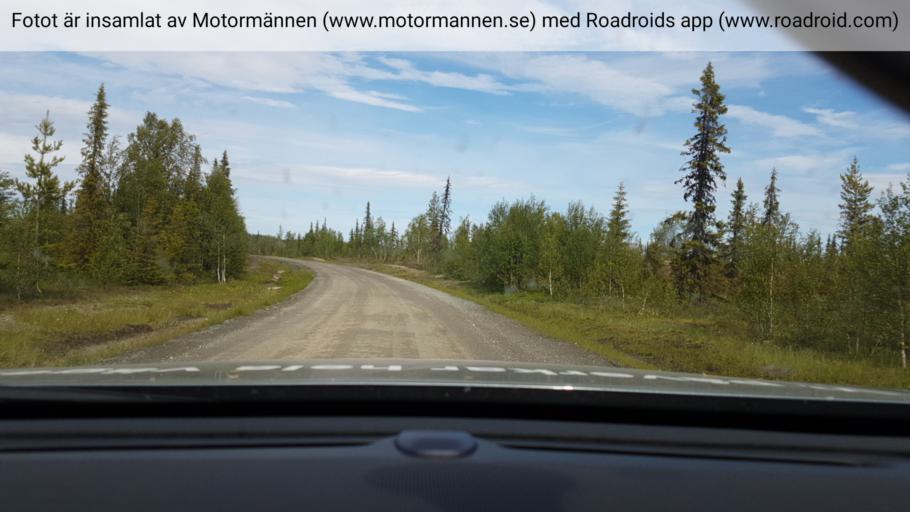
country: SE
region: Vaesterbotten
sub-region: Vilhelmina Kommun
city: Sjoberg
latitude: 65.1651
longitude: 16.3470
